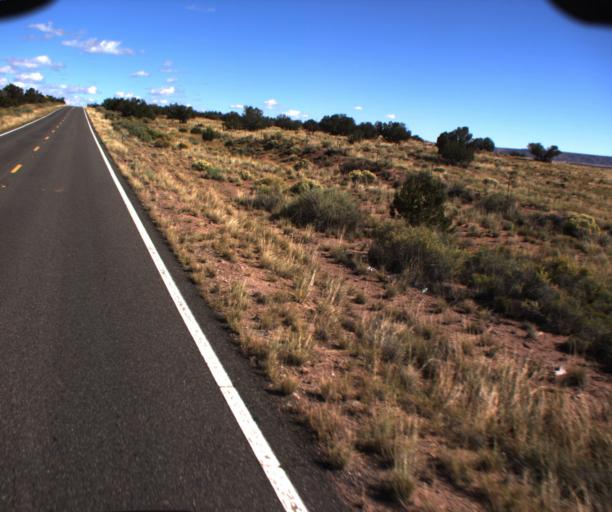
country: US
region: Arizona
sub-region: Apache County
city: Saint Johns
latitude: 34.7241
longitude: -109.2578
